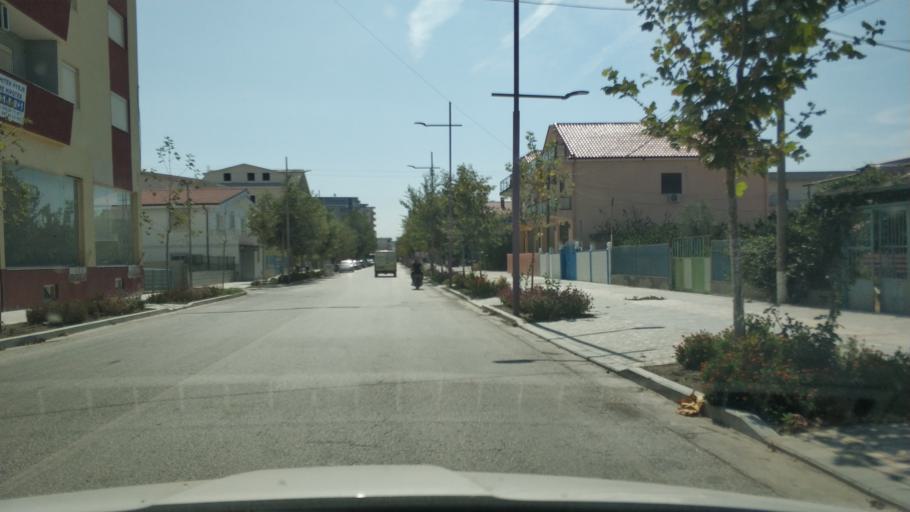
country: AL
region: Fier
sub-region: Rrethi i Lushnjes
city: Divjake
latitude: 40.9990
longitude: 19.5317
